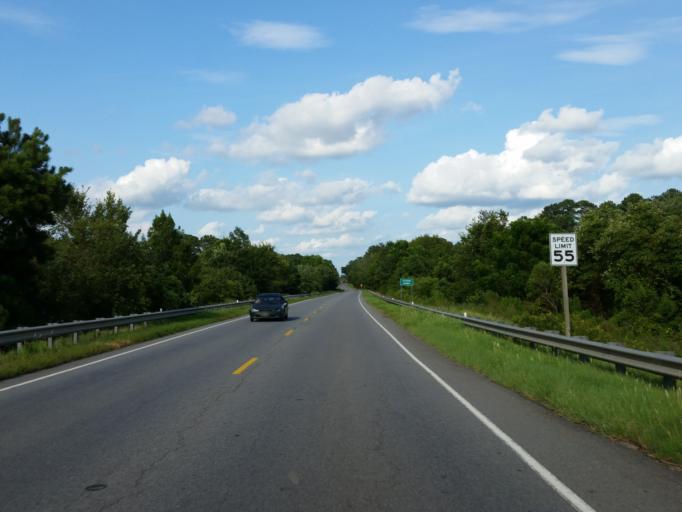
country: US
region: Georgia
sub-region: Crisp County
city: Cordele
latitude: 31.9657
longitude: -83.9276
